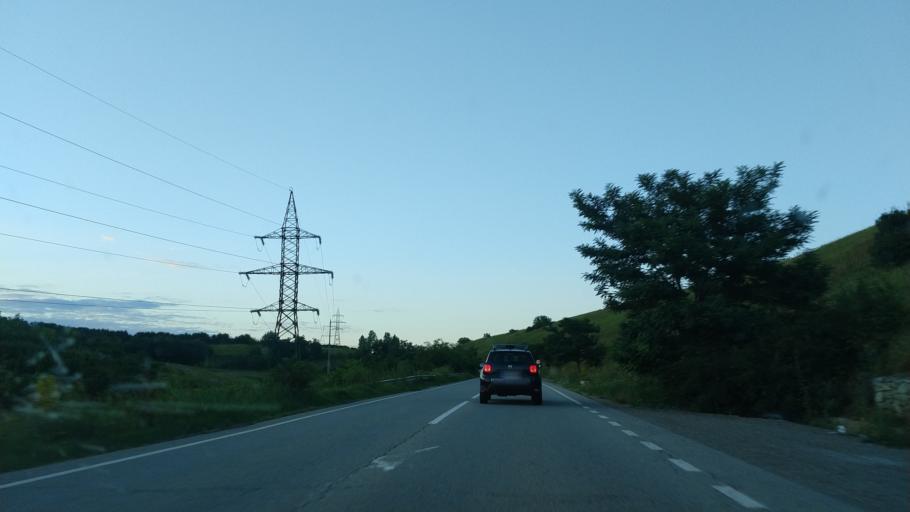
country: RO
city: Vanatori
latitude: 47.2678
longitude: 27.5475
